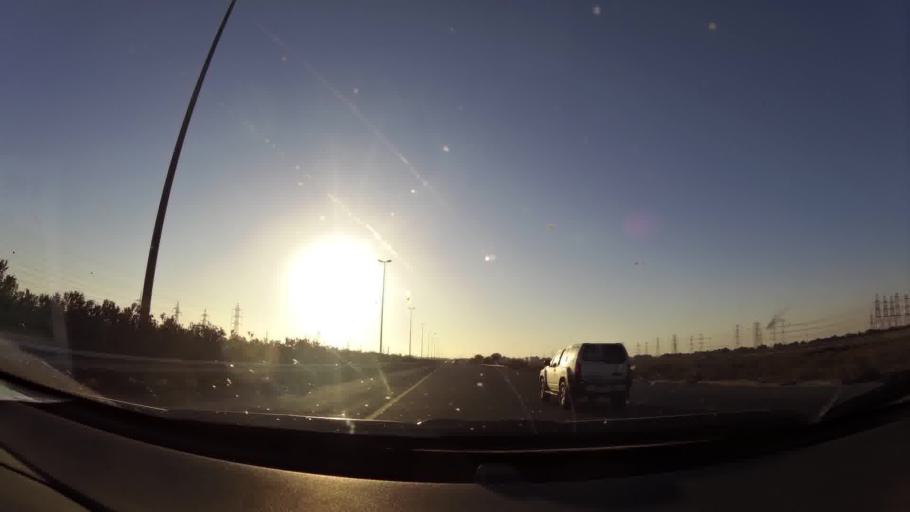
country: KW
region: Al Ahmadi
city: Al Fahahil
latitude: 28.9302
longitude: 48.1969
